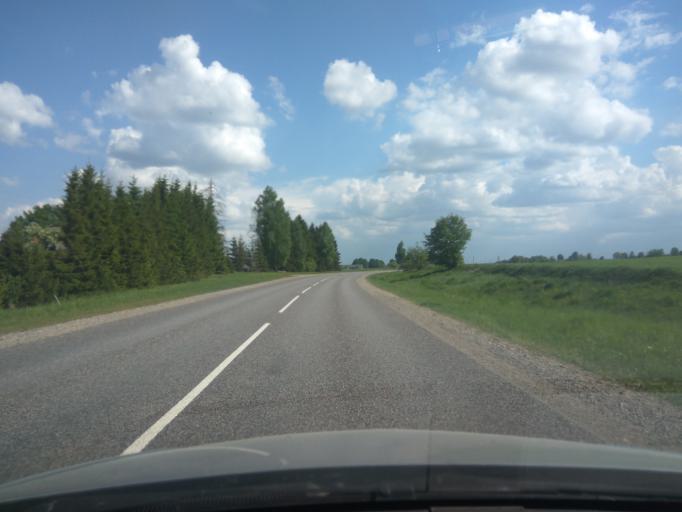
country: LV
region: Kuldigas Rajons
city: Kuldiga
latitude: 57.0184
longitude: 21.8737
